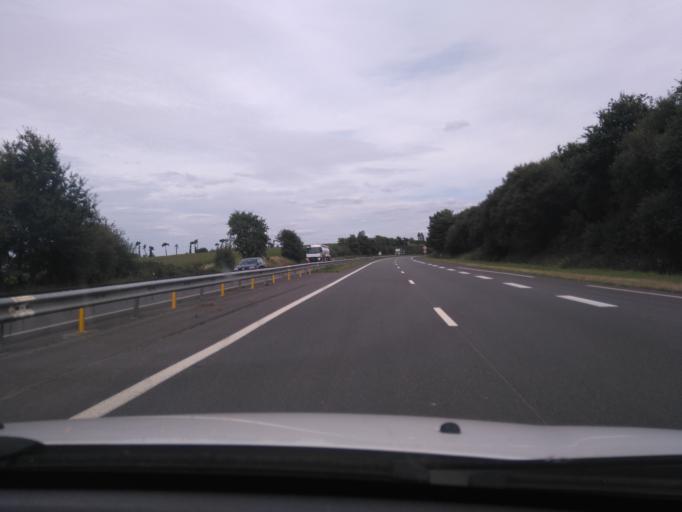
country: FR
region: Brittany
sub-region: Departement des Cotes-d'Armor
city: Caulnes
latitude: 48.2724
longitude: -2.1676
